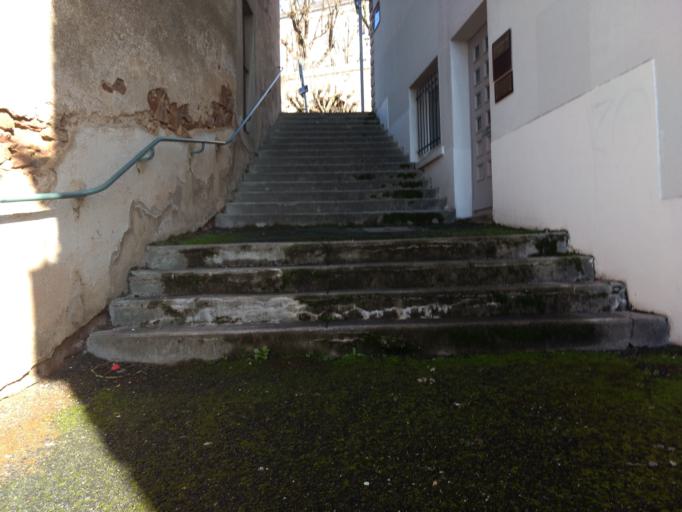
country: FR
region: Midi-Pyrenees
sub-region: Departement de l'Aveyron
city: Rodez
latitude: 44.3483
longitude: 2.5715
